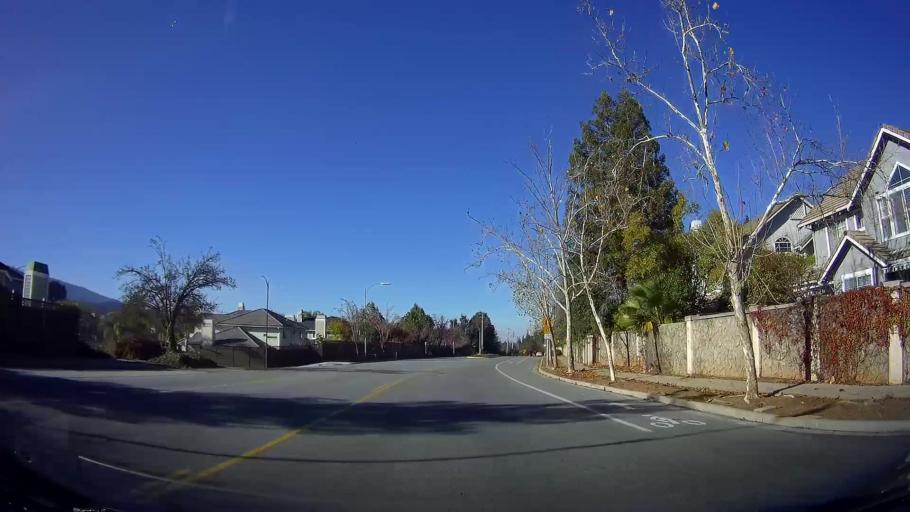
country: US
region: California
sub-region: Santa Clara County
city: Seven Trees
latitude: 37.2022
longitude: -121.8391
